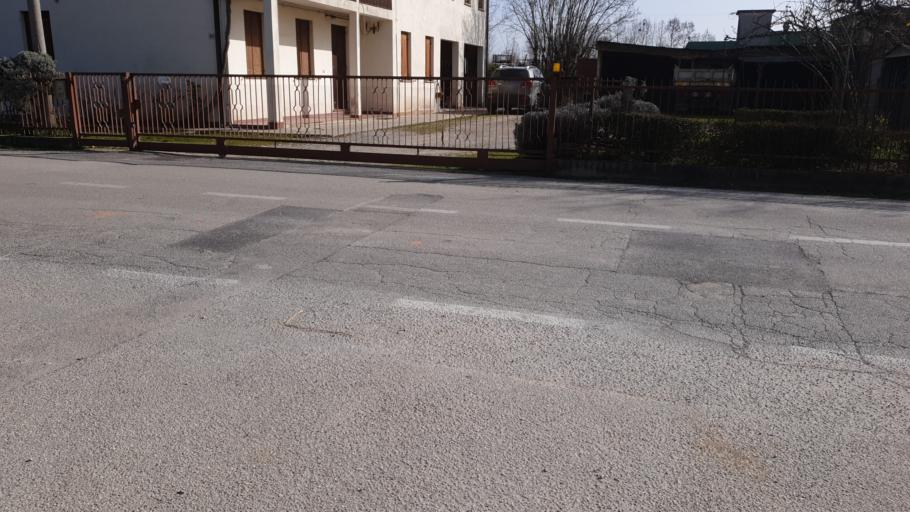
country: IT
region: Veneto
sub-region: Provincia di Padova
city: Campodarsego
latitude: 45.4779
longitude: 11.9169
